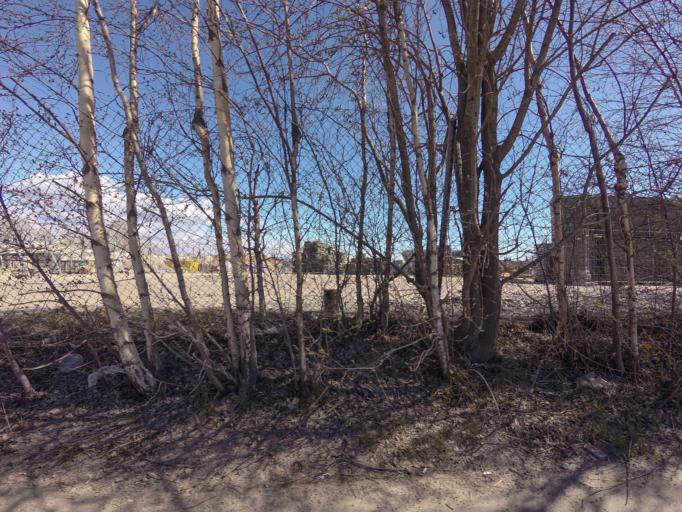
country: FI
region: Uusimaa
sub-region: Helsinki
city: Helsinki
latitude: 60.1917
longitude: 24.9815
